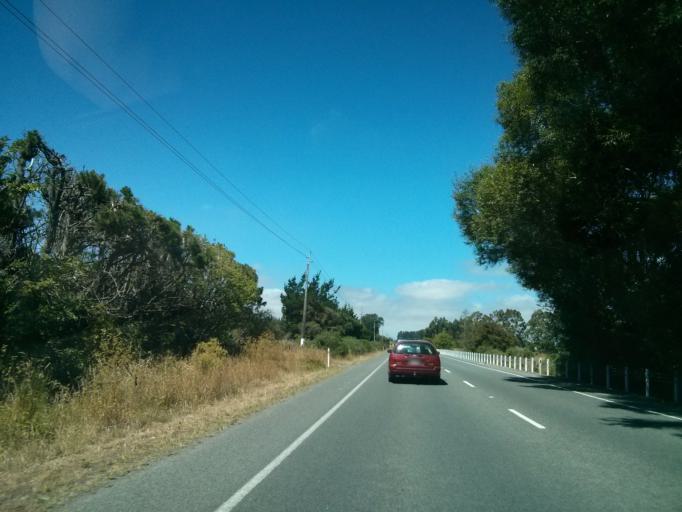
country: NZ
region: Canterbury
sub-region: Waimakariri District
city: Kaiapoi
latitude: -43.3919
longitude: 172.5833
